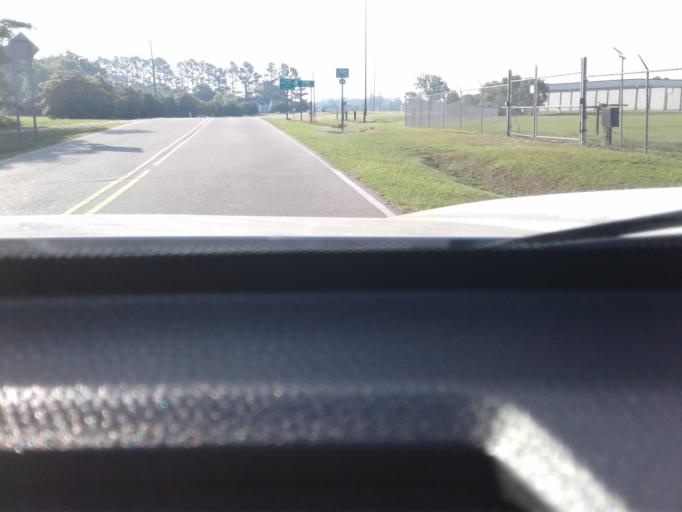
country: US
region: North Carolina
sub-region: Harnett County
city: Dunn
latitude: 35.3257
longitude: -78.6297
